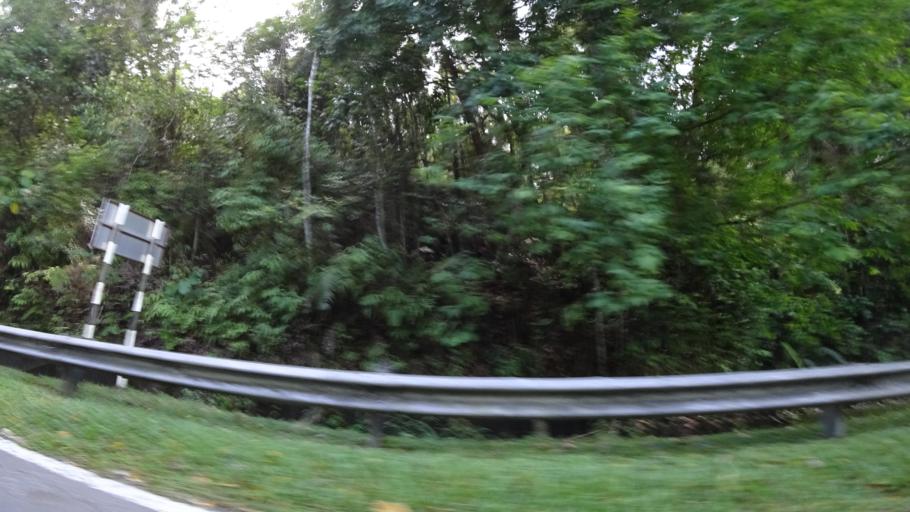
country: BN
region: Brunei and Muara
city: Bandar Seri Begawan
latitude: 4.8866
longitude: 114.9698
